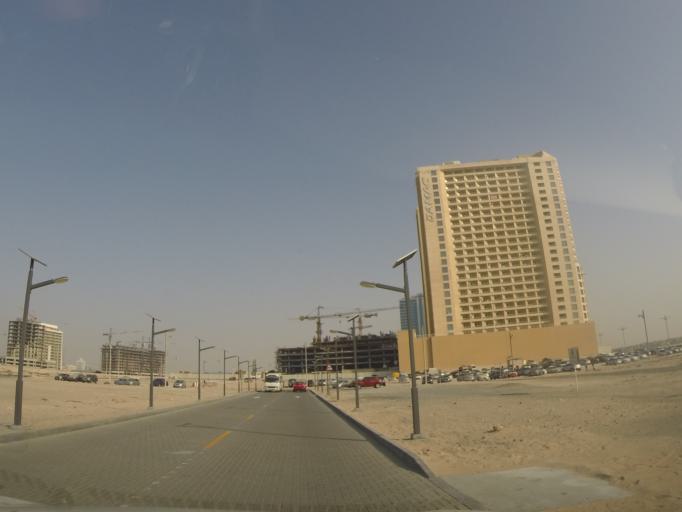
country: AE
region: Dubai
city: Dubai
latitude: 25.0385
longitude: 55.2003
